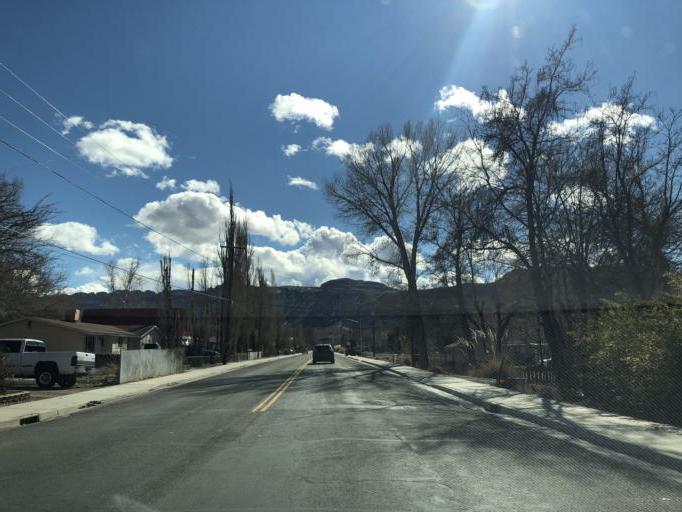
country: US
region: Utah
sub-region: Grand County
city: Moab
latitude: 38.5860
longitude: -109.5611
